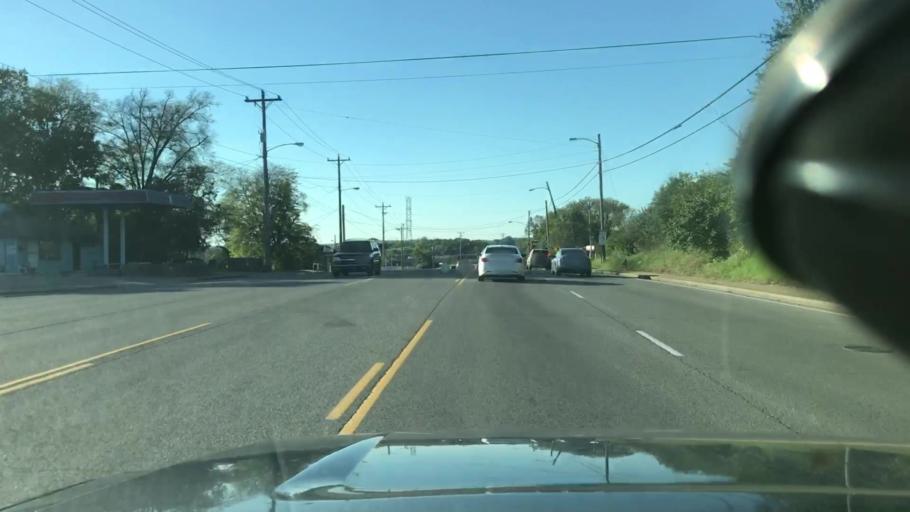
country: US
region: Tennessee
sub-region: Davidson County
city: Nashville
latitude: 36.1953
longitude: -86.8338
